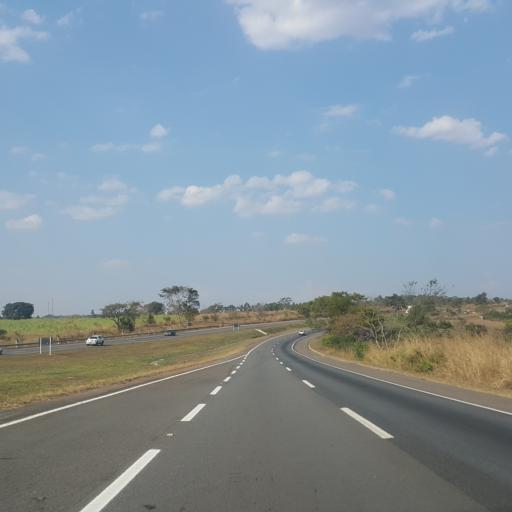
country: BR
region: Goias
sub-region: Abadiania
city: Abadiania
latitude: -16.1146
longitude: -48.5467
